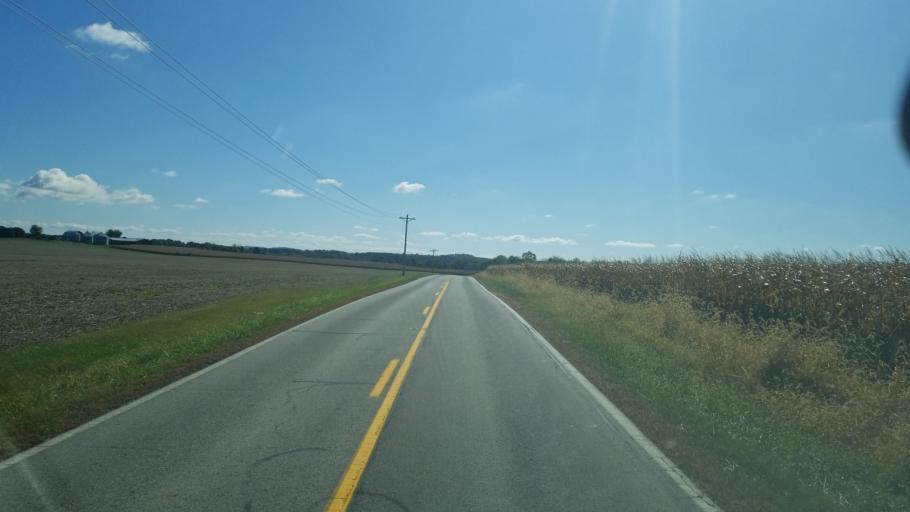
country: US
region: Ohio
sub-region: Highland County
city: Leesburg
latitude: 39.2842
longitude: -83.4995
